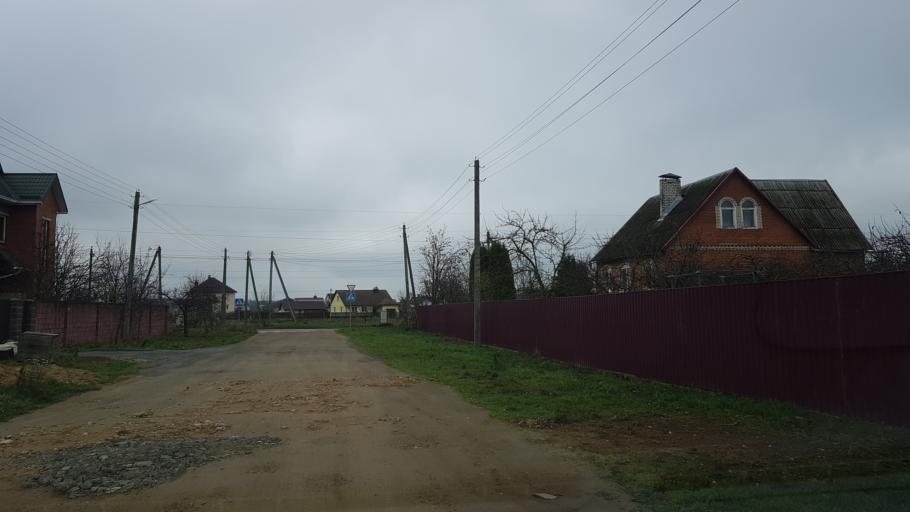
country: BY
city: Fanipol
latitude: 53.7334
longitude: 27.3191
